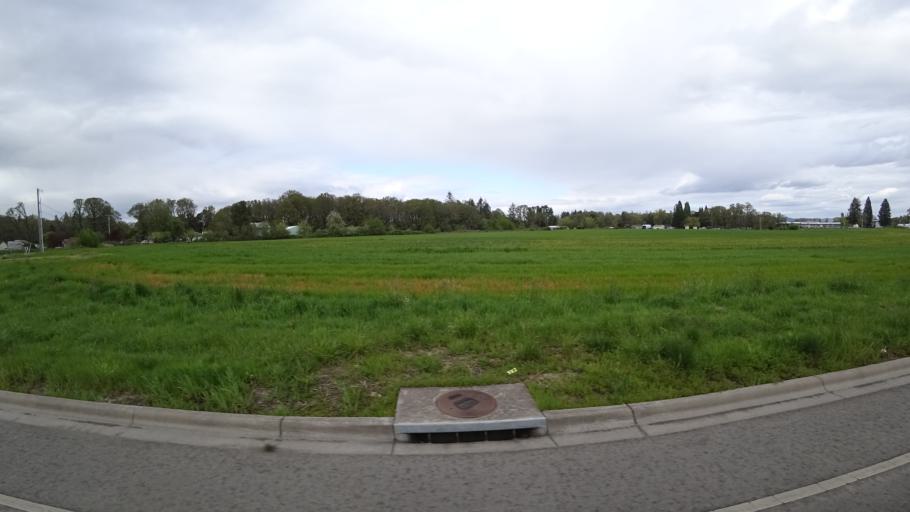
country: US
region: Oregon
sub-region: Washington County
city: Hillsboro
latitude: 45.5522
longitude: -122.9580
